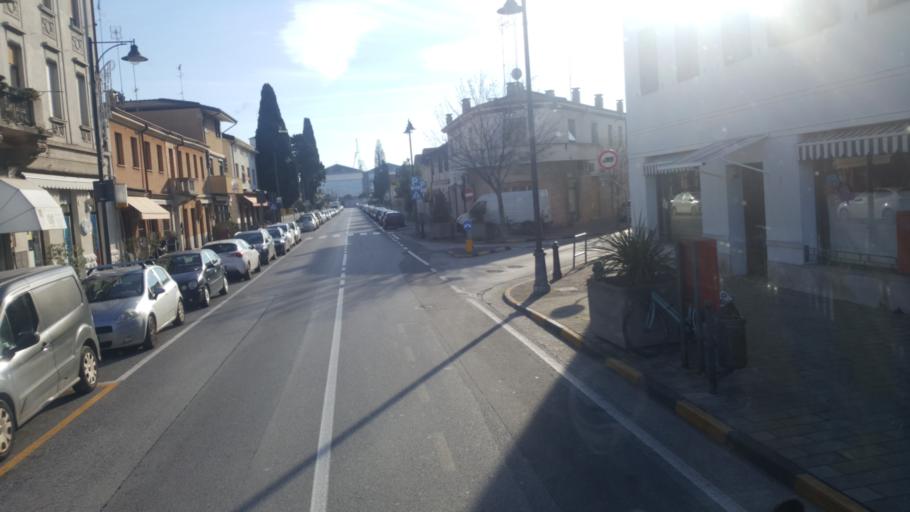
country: IT
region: Friuli Venezia Giulia
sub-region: Provincia di Gorizia
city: Monfalcone
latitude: 45.7991
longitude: 13.5332
